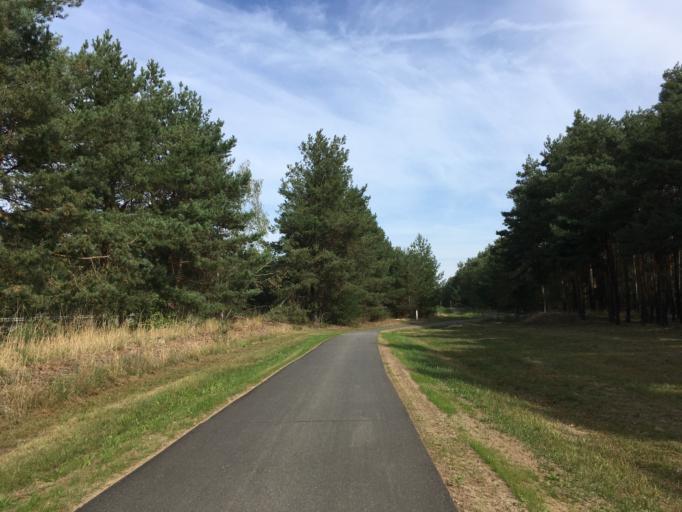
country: DE
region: Brandenburg
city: Heinersbruck
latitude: 51.8242
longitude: 14.5841
